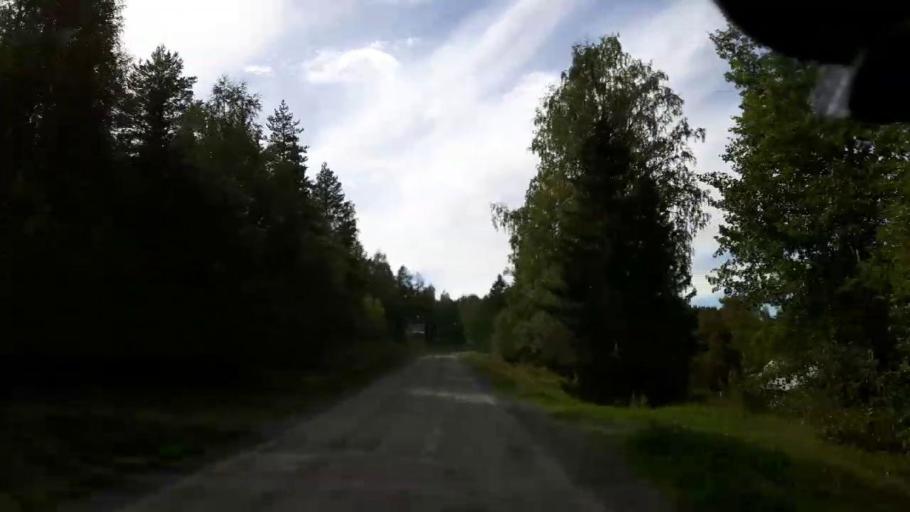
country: SE
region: Jaemtland
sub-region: Ragunda Kommun
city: Hammarstrand
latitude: 63.1379
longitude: 16.1904
